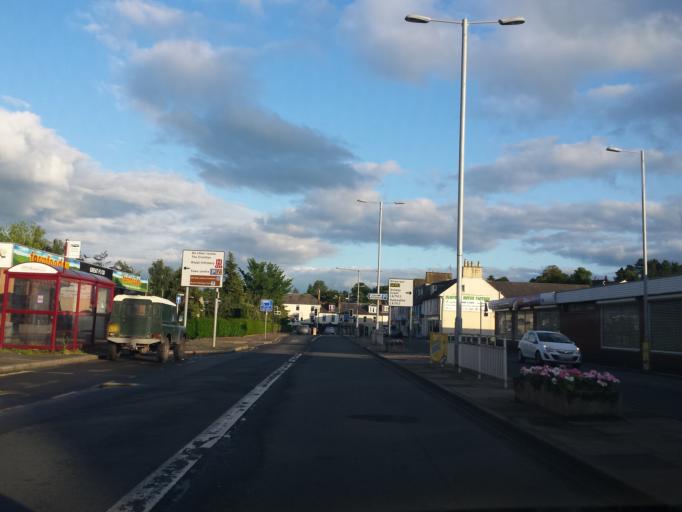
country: GB
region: Scotland
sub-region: Dumfries and Galloway
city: Dumfries
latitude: 55.0699
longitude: -3.6196
